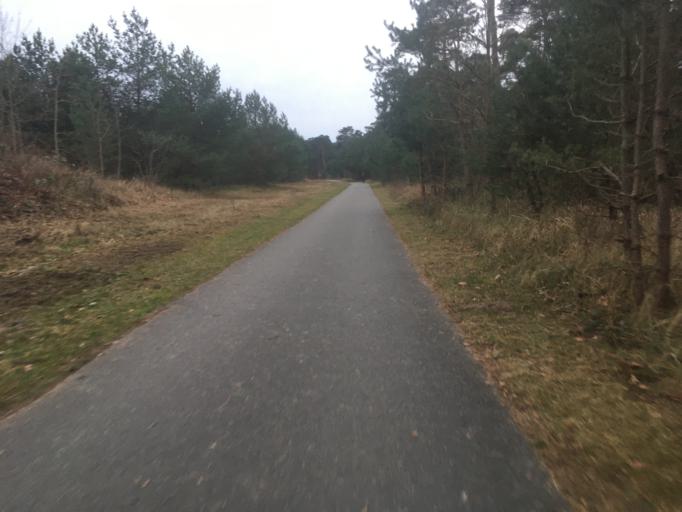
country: DE
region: Mecklenburg-Vorpommern
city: Sagard
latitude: 54.4737
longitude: 13.5687
